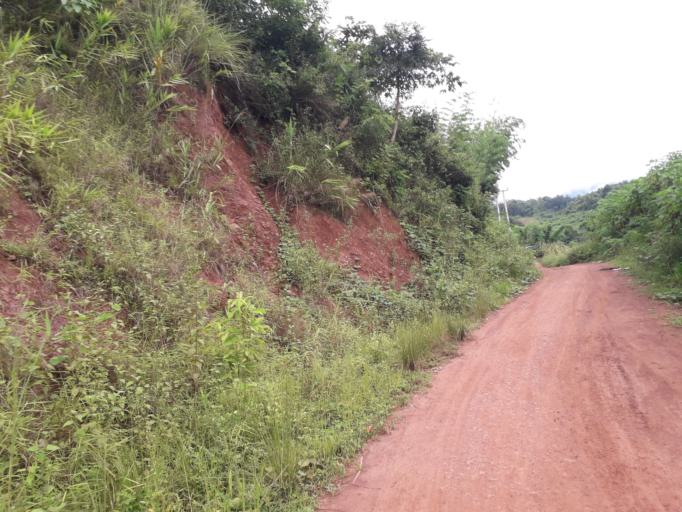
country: CN
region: Yunnan
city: Menglie
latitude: 22.2435
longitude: 101.6095
